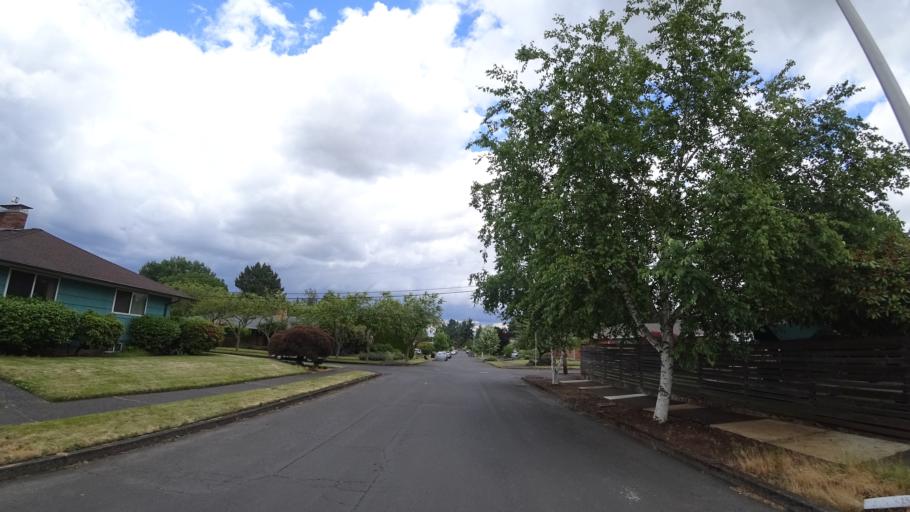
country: US
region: Oregon
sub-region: Multnomah County
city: Portland
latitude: 45.5605
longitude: -122.6120
